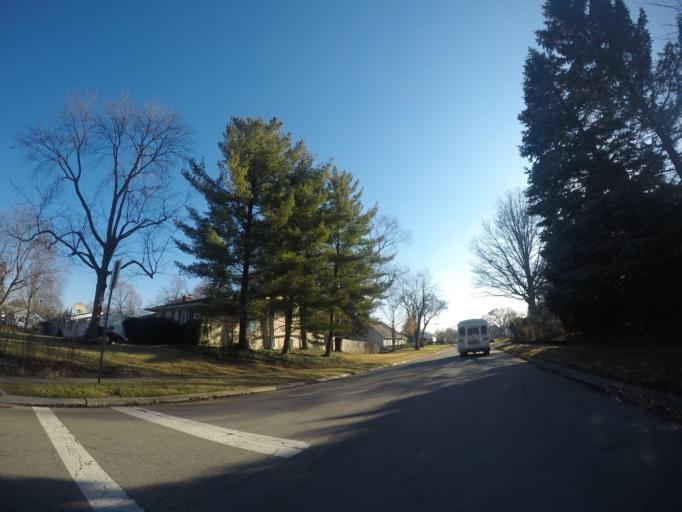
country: US
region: Ohio
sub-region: Franklin County
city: Upper Arlington
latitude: 40.0410
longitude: -83.0812
